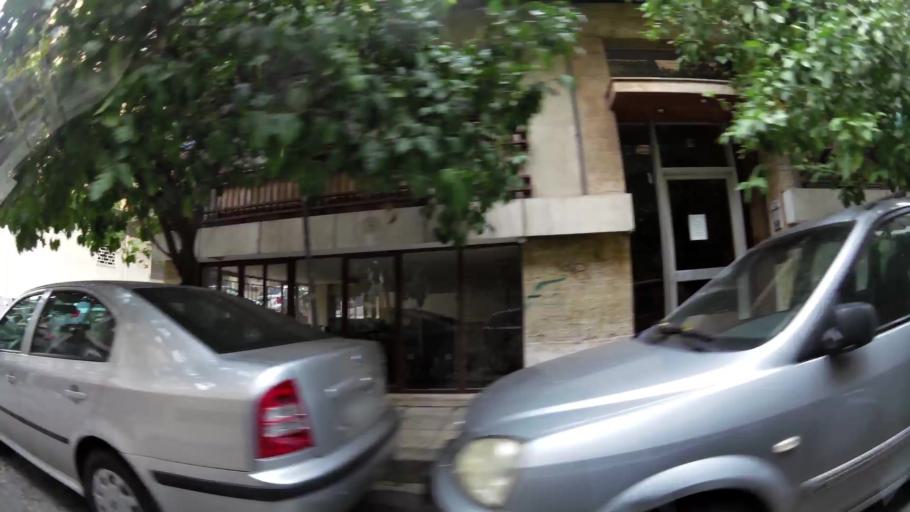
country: GR
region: Attica
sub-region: Nomos Attikis
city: Piraeus
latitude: 37.9305
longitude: 23.6434
